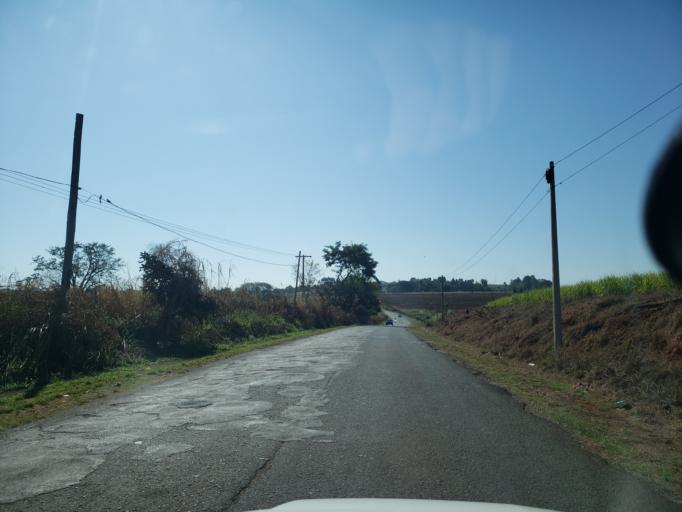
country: BR
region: Sao Paulo
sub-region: Moji-Guacu
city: Mogi-Gaucu
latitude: -22.3527
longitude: -46.8994
